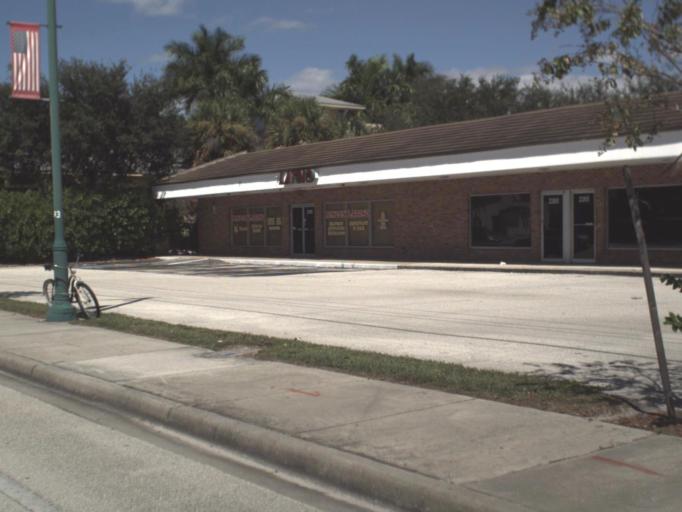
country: US
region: Florida
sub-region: Collier County
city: Naples
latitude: 26.1342
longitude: -81.7765
